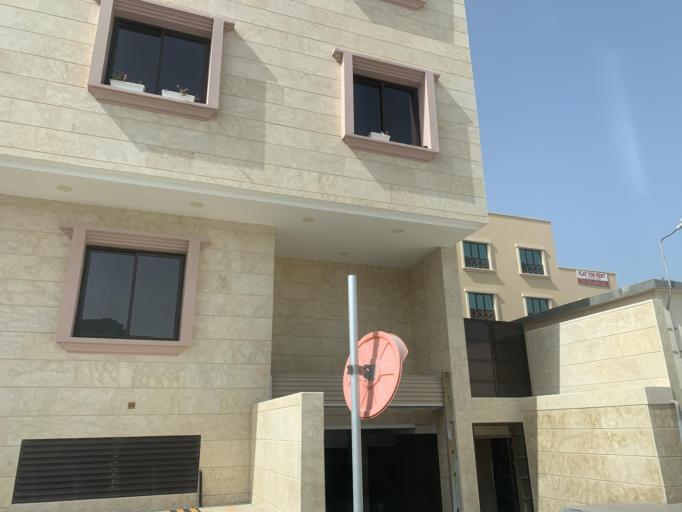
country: BH
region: Northern
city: Ar Rifa'
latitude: 26.1426
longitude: 50.5727
